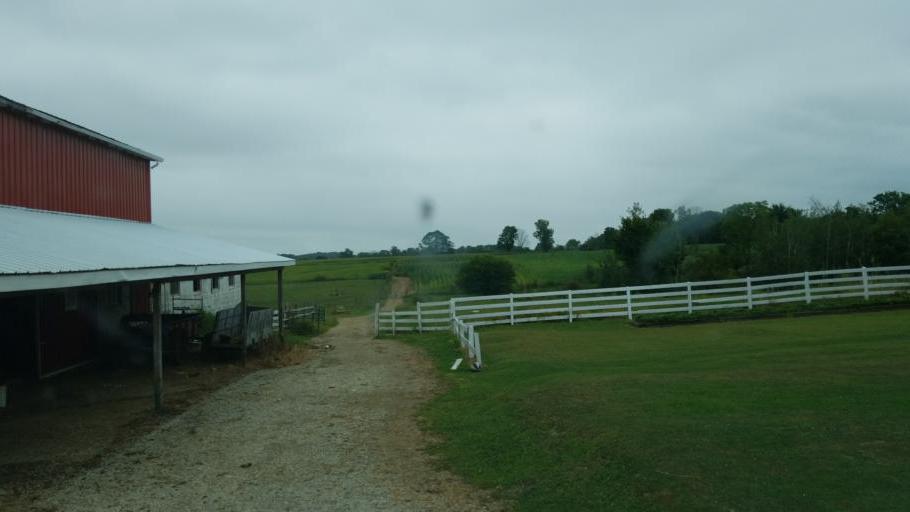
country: US
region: Ohio
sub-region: Knox County
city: Fredericktown
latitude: 40.5018
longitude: -82.6135
